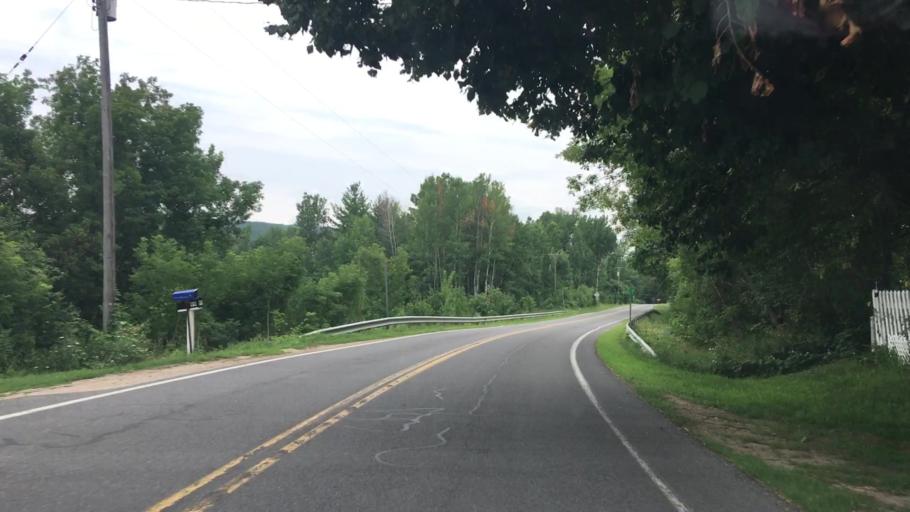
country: US
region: New York
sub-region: Clinton County
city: Peru
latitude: 44.5292
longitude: -73.5733
